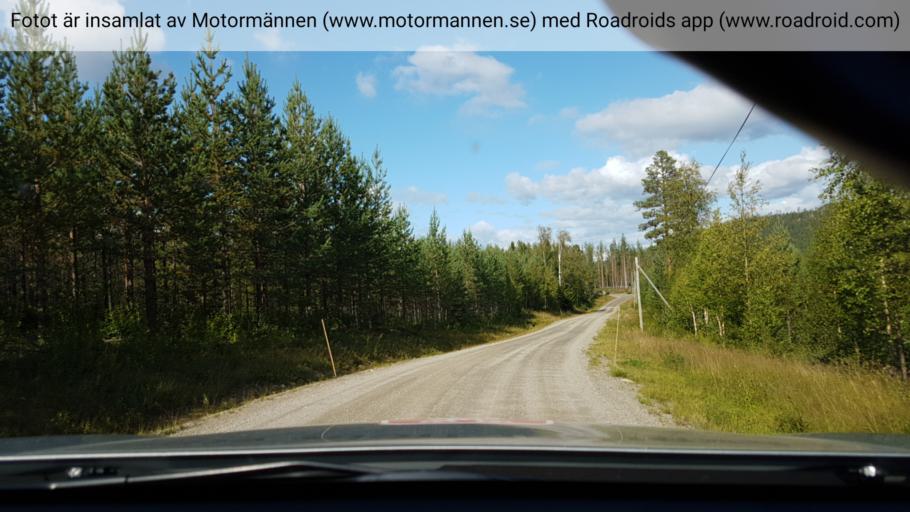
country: SE
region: Vaesterbotten
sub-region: Lycksele Kommun
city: Lycksele
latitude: 64.5781
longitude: 19.0174
